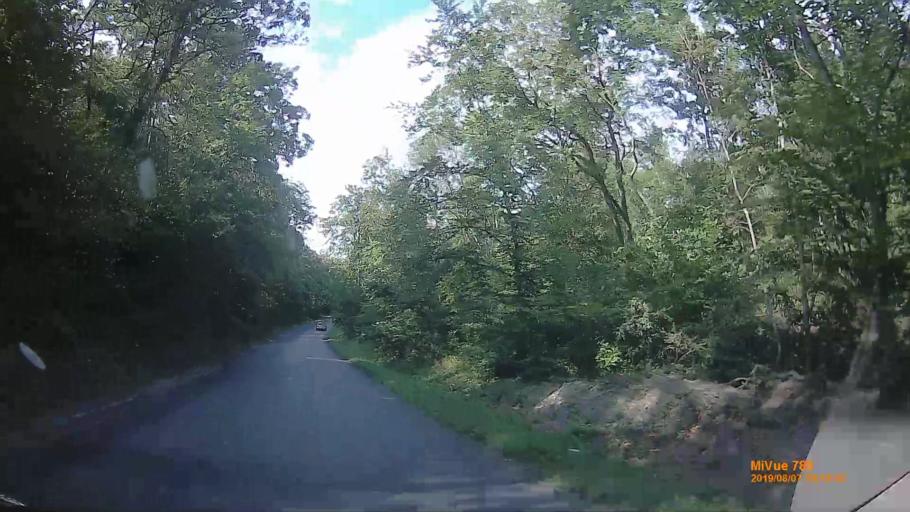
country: HU
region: Zala
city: Cserszegtomaj
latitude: 46.8465
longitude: 17.2672
